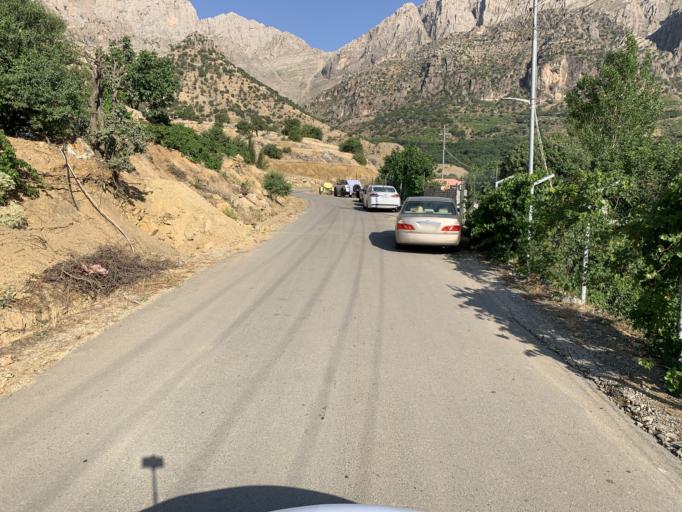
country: IQ
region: As Sulaymaniyah
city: Qeladize
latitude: 35.9917
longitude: 45.1987
